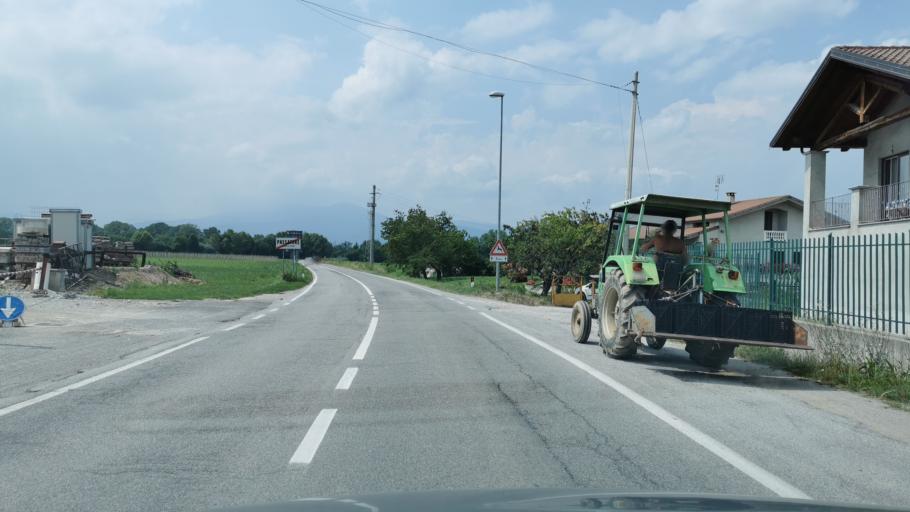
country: IT
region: Piedmont
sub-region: Provincia di Cuneo
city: Roata Rossi
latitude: 44.4331
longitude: 7.5041
